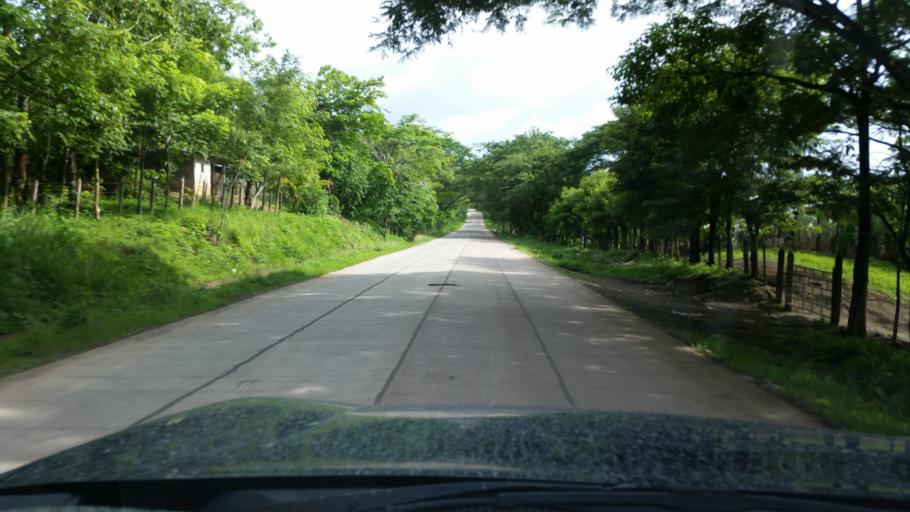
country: NI
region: Atlantico Norte (RAAN)
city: Siuna
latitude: 13.5820
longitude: -84.8142
